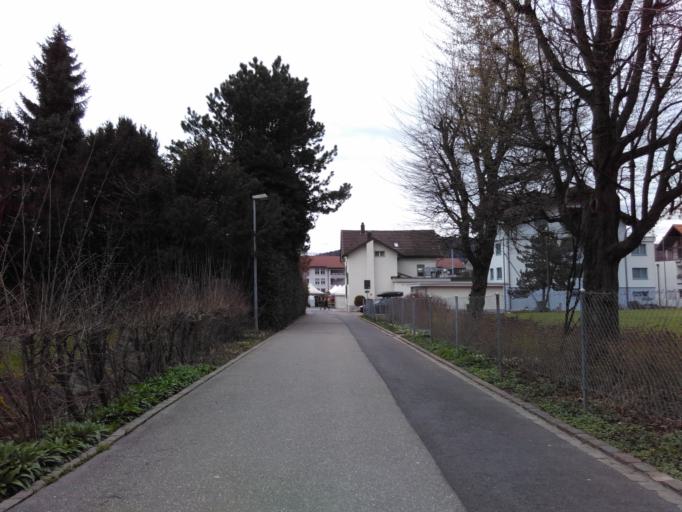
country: CH
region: Schwyz
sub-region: Bezirk March
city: Schubelbach
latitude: 47.1818
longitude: 8.8997
